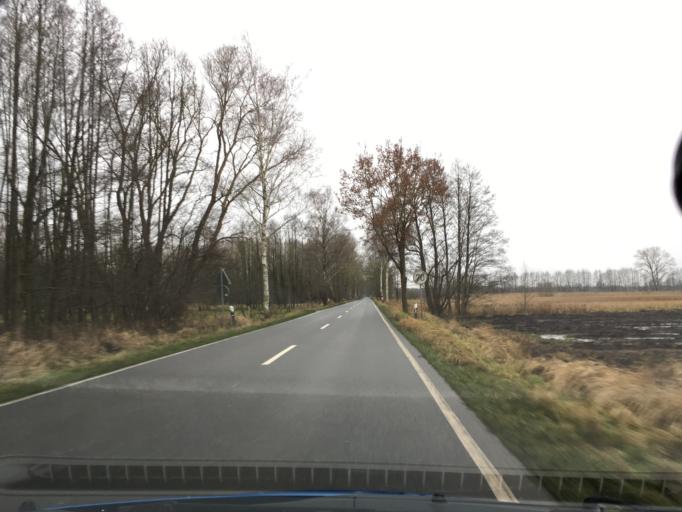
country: DE
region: Lower Saxony
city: Neetze
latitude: 53.3093
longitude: 10.6668
